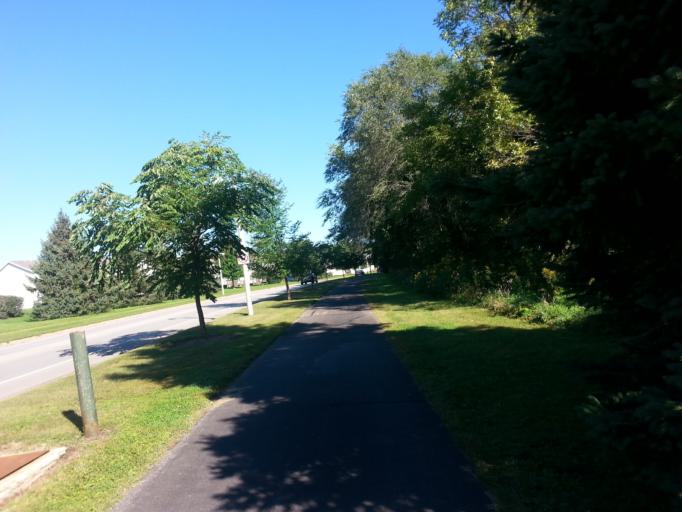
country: US
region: Minnesota
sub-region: Olmsted County
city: Rochester
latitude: 44.0542
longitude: -92.4668
